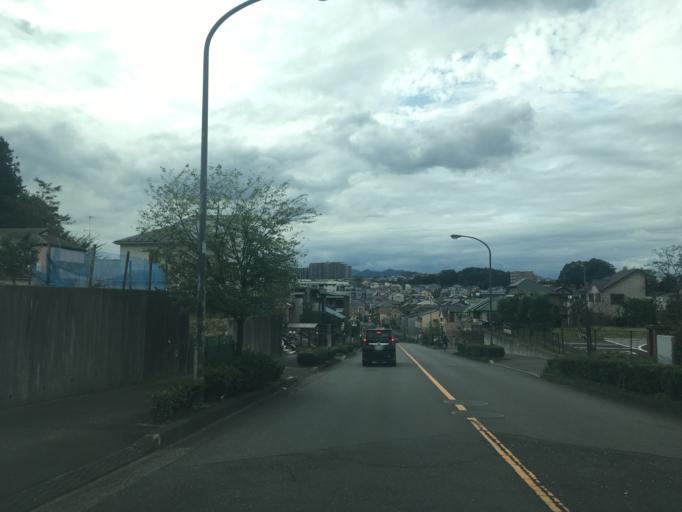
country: JP
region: Tokyo
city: Hachioji
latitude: 35.6263
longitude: 139.3324
